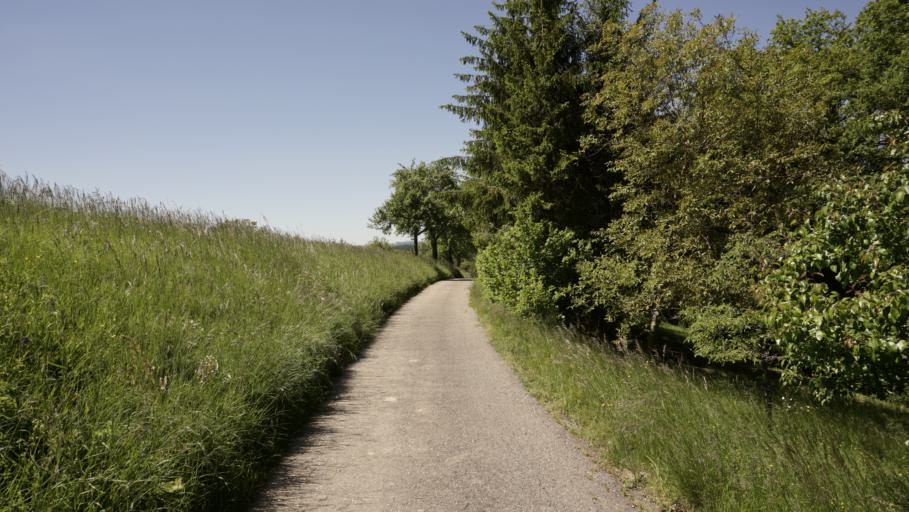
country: DE
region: Baden-Wuerttemberg
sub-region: Karlsruhe Region
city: Mosbach
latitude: 49.3744
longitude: 9.1795
